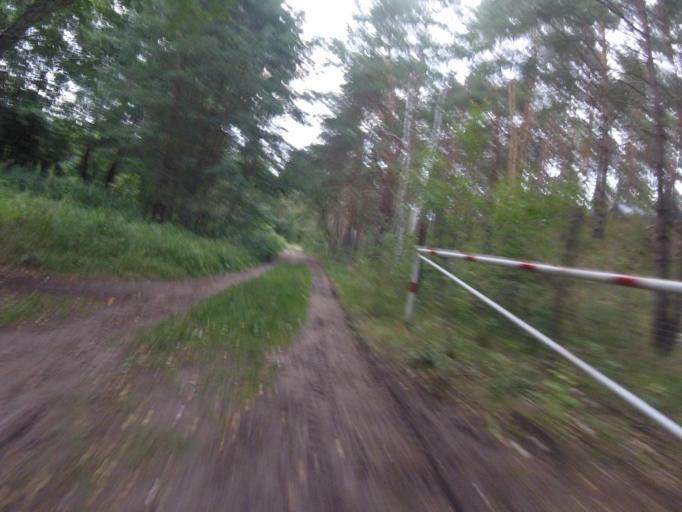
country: DE
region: Brandenburg
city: Gross Koris
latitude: 52.1567
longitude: 13.6815
